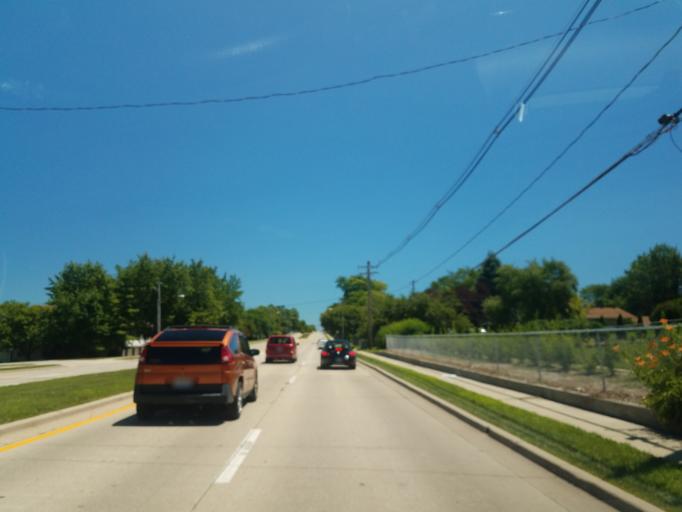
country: US
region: Illinois
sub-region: McLean County
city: Normal
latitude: 40.5103
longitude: -88.9668
